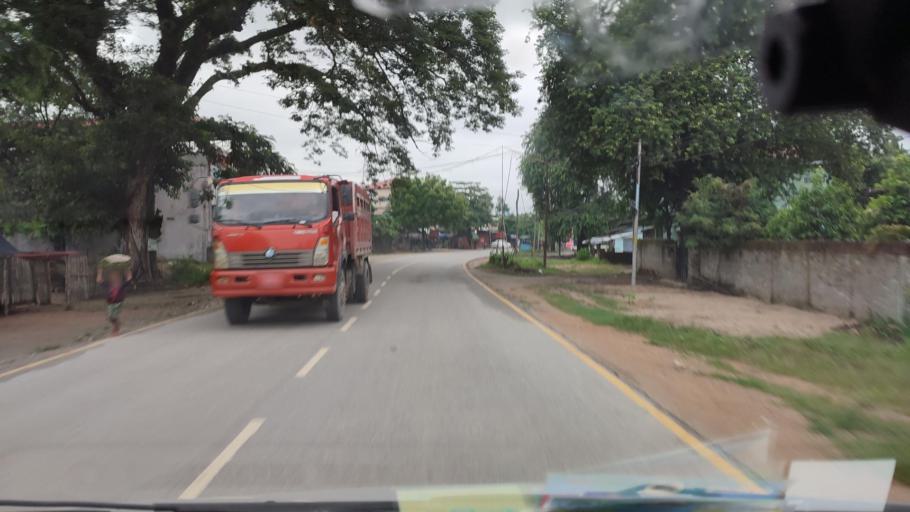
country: MM
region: Bago
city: Taungoo
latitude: 18.9470
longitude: 96.4619
